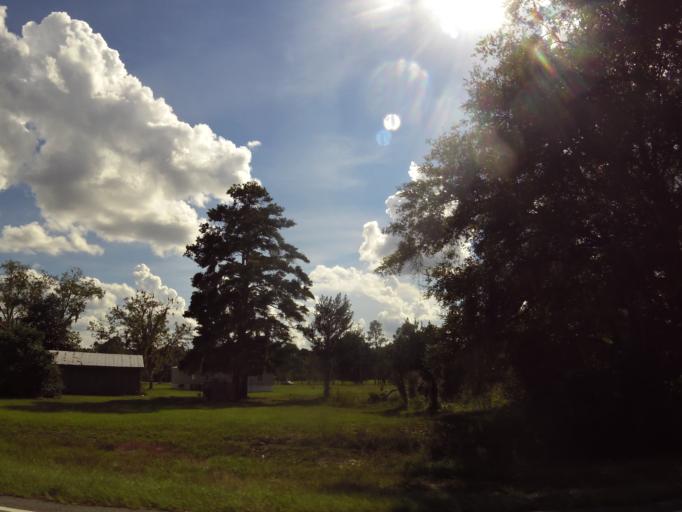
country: US
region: Georgia
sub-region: Echols County
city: Statenville
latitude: 30.7714
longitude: -83.1407
